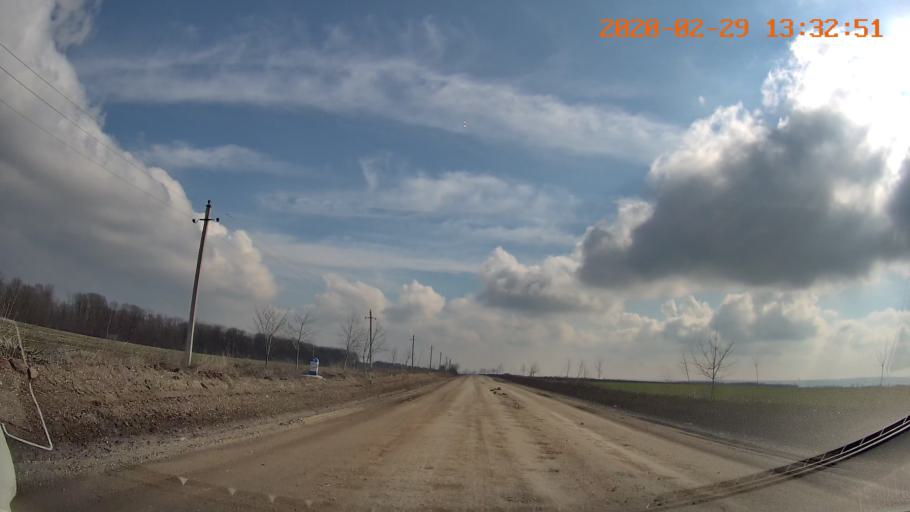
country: MD
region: Telenesti
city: Camenca
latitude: 47.8769
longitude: 28.6124
